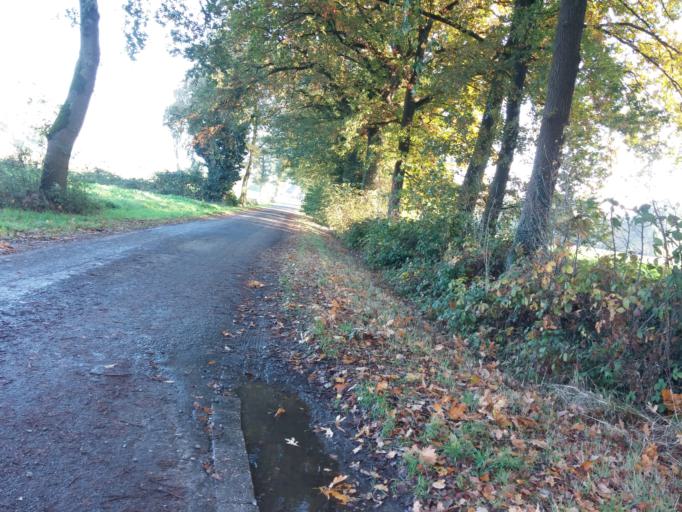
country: DE
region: North Rhine-Westphalia
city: Dorsten
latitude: 51.6412
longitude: 6.9781
